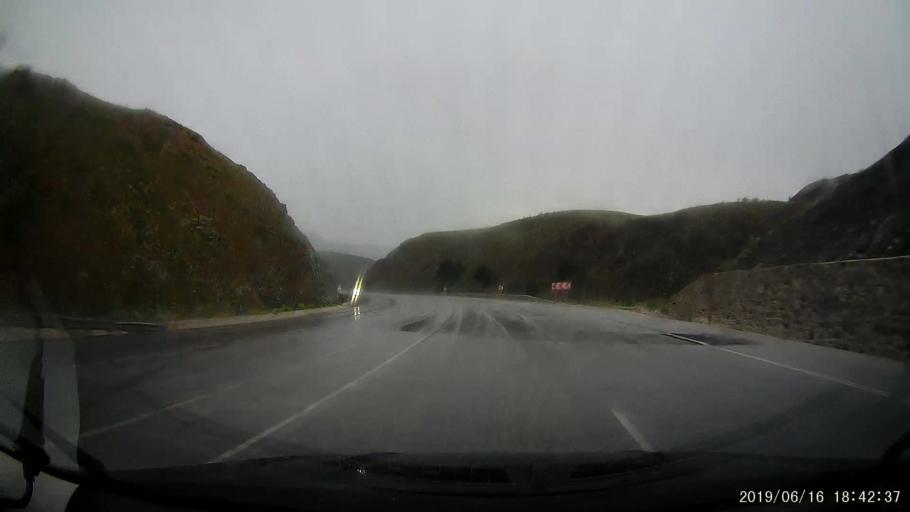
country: TR
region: Erzincan
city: Doganbeyli
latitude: 39.8682
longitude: 39.1058
